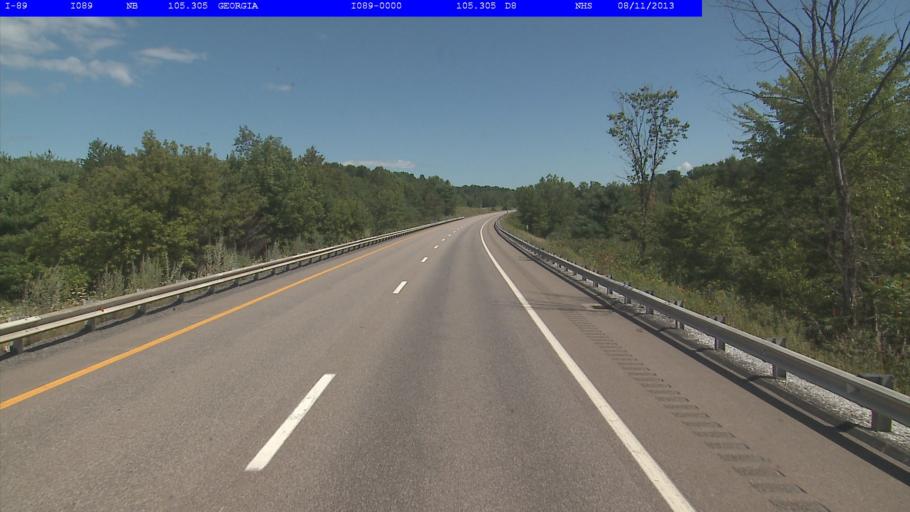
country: US
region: Vermont
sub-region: Chittenden County
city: Milton
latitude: 44.6887
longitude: -73.1261
